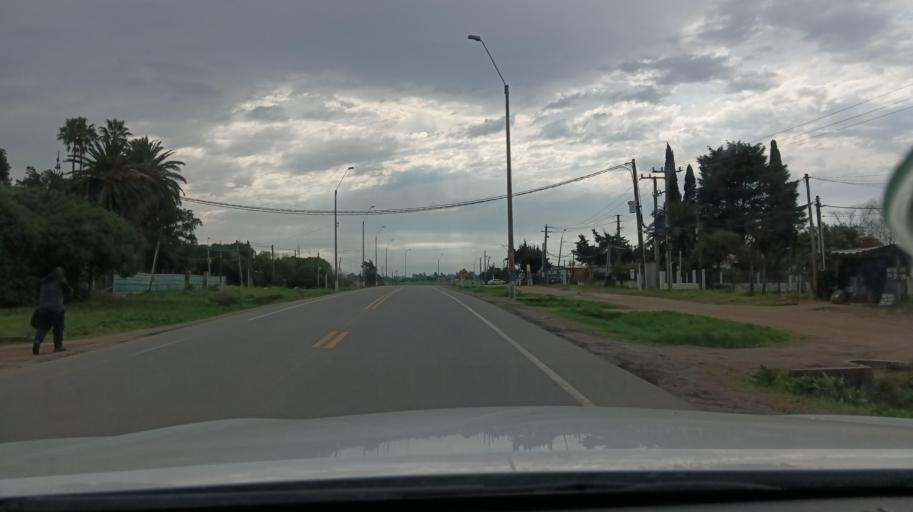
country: UY
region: Canelones
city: Toledo
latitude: -34.7475
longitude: -56.1108
